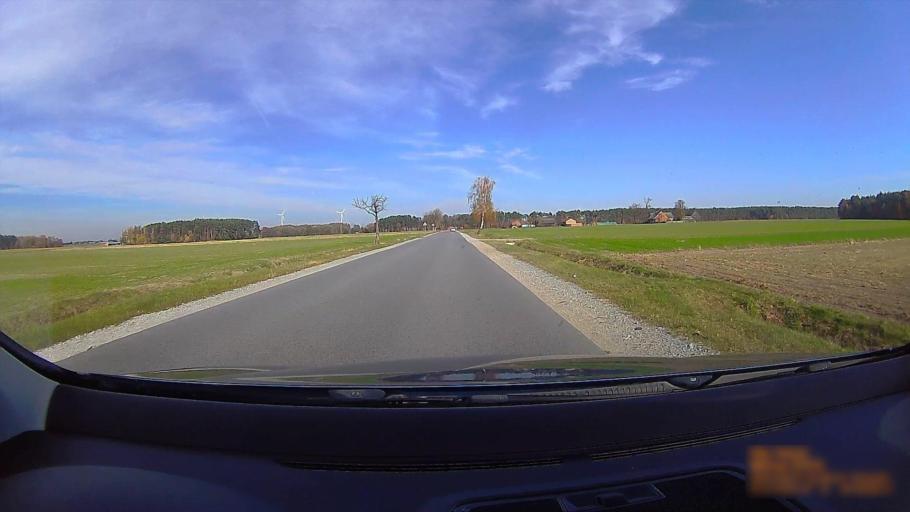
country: PL
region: Greater Poland Voivodeship
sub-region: Powiat ostrzeszowski
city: Doruchow
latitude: 51.3802
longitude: 18.0433
